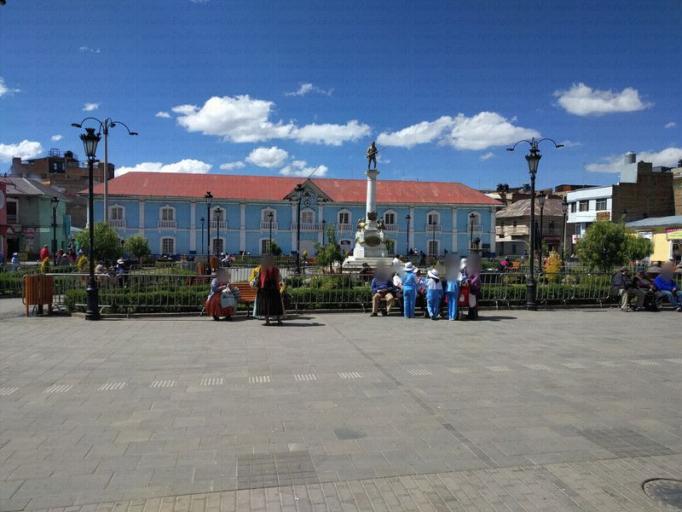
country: PE
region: Puno
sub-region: Provincia de Puno
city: Puno
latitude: -15.8377
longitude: -70.0283
